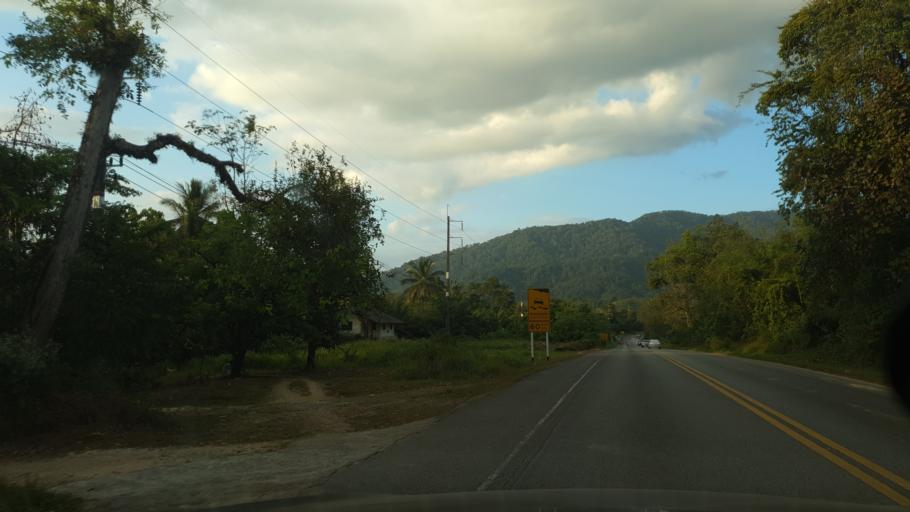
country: TH
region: Phangnga
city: Takua Pa
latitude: 8.9149
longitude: 98.4087
